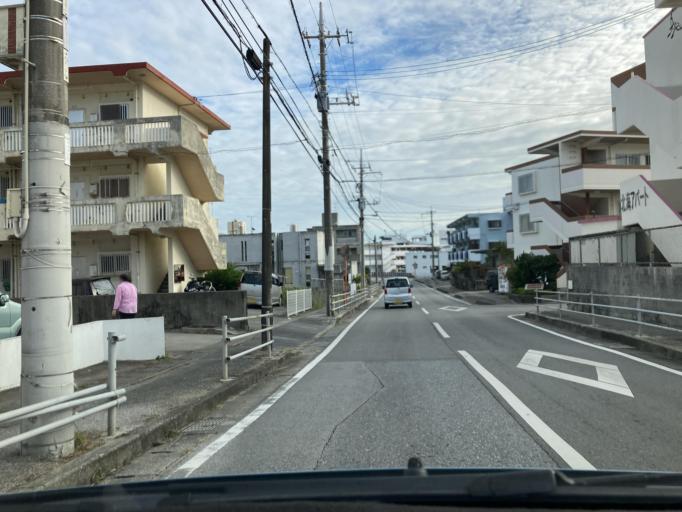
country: JP
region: Okinawa
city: Tomigusuku
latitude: 26.2001
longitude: 127.7318
